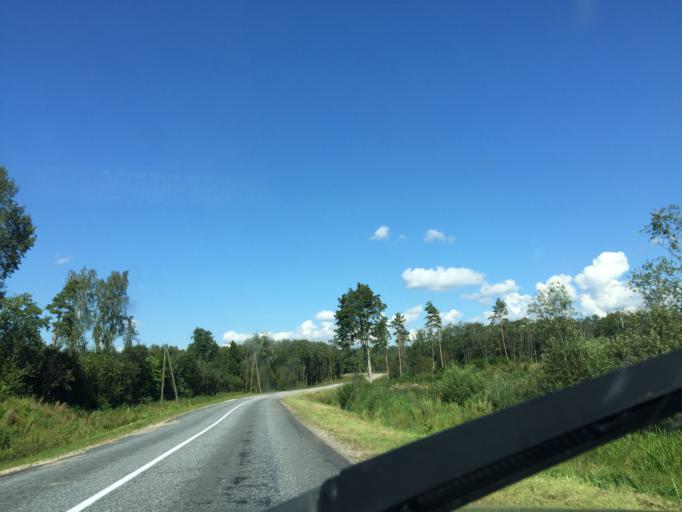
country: LV
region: Limbazu Rajons
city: Limbazi
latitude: 57.4385
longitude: 24.7189
